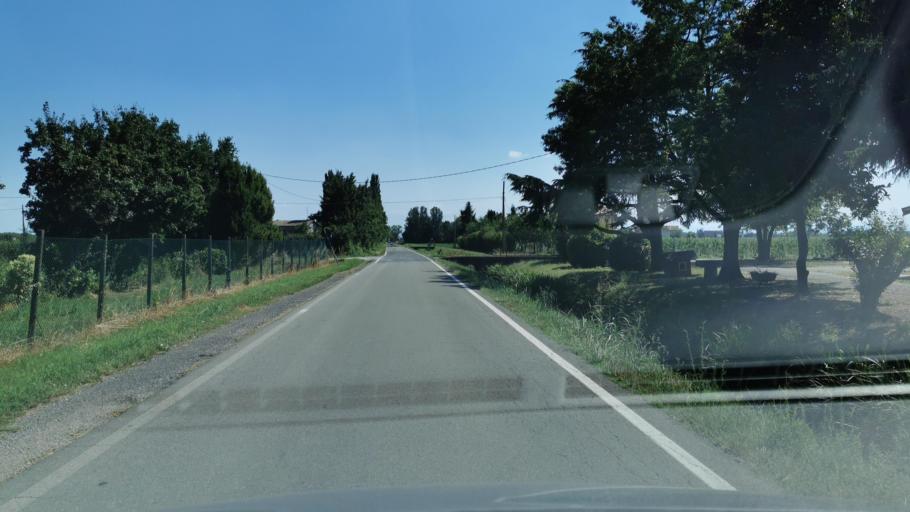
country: IT
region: Emilia-Romagna
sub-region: Provincia di Modena
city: Limidi
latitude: 44.7781
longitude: 10.9183
